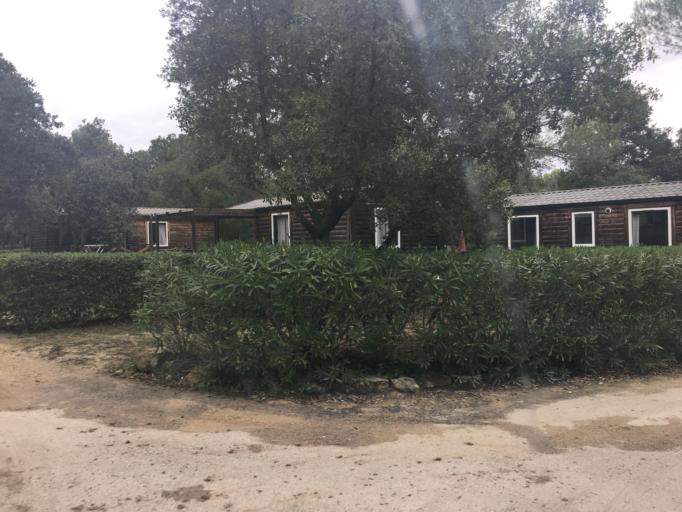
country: FR
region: Languedoc-Roussillon
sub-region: Departement du Gard
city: Sommieres
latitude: 43.7666
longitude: 4.0992
